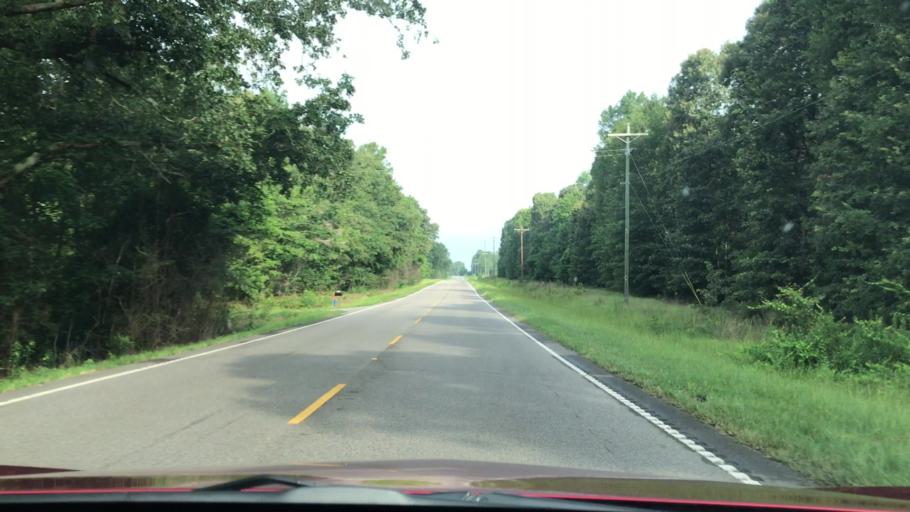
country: US
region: South Carolina
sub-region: Lexington County
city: Leesville
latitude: 33.6812
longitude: -81.4452
